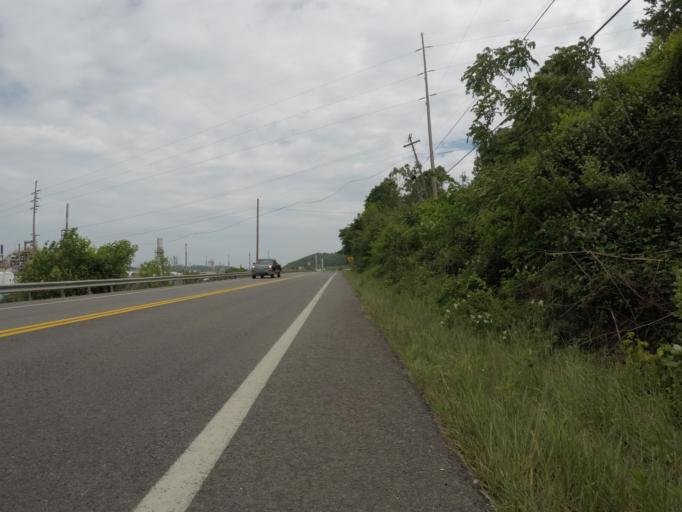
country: US
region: West Virginia
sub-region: Wayne County
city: Kenova
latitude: 38.3669
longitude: -82.5924
